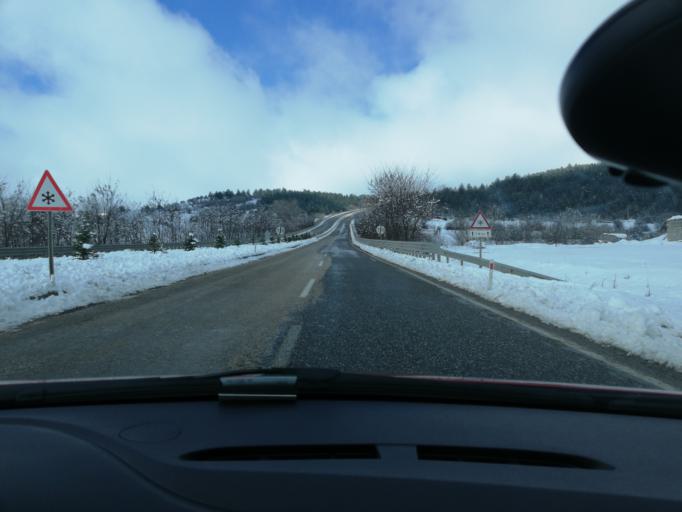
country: TR
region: Kastamonu
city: Ihsangazi
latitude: 41.3053
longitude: 33.5888
